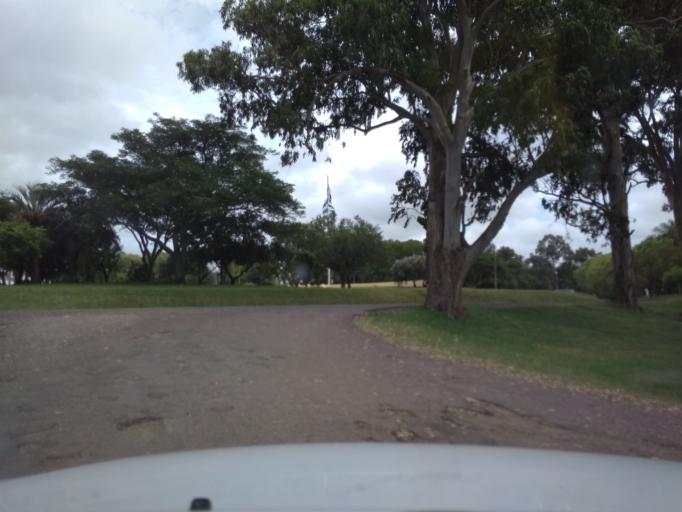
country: UY
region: Florida
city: Florida
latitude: -34.1013
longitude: -56.2035
